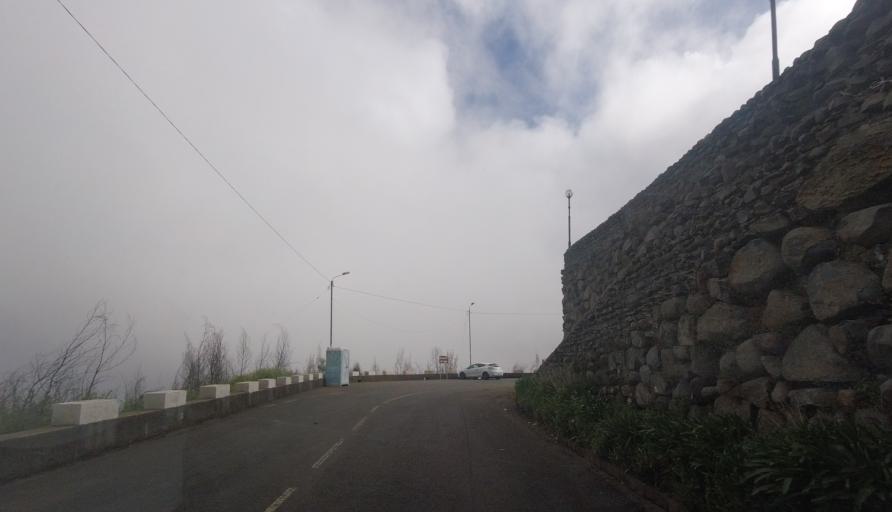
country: PT
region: Madeira
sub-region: Funchal
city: Nossa Senhora do Monte
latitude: 32.6845
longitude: -16.8987
